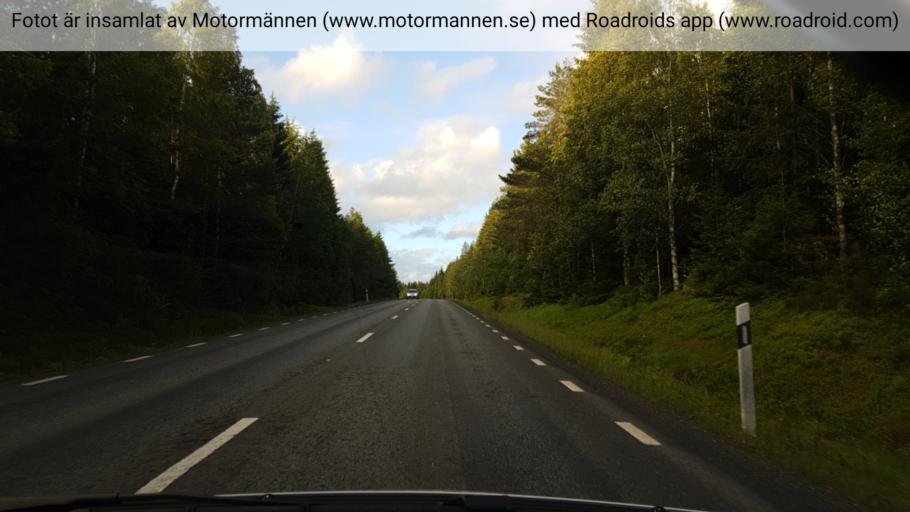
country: SE
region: OErebro
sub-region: Karlskoga Kommun
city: Karlskoga
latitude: 59.4240
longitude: 14.7041
